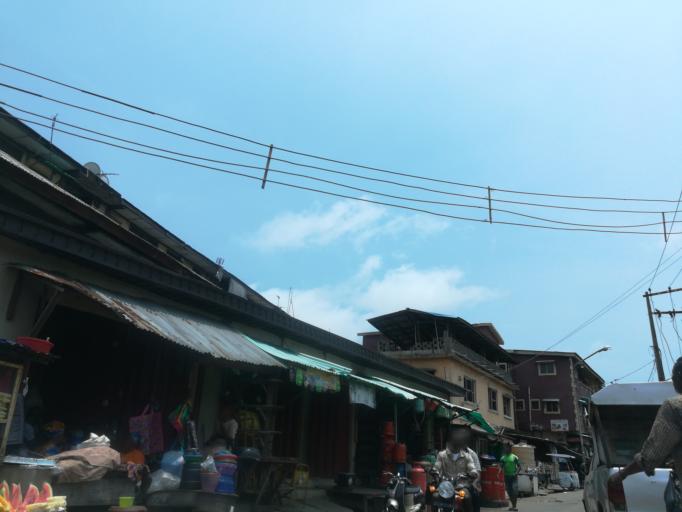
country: NG
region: Lagos
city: Lagos
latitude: 6.4565
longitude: 3.3978
